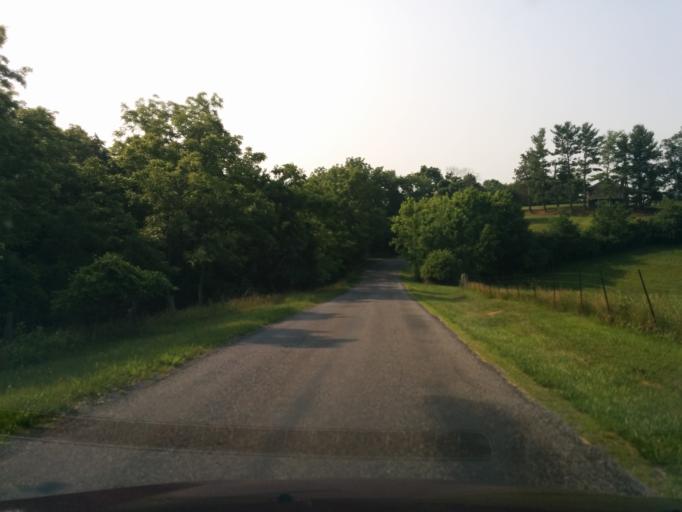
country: US
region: Virginia
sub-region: City of Lexington
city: Lexington
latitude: 37.7572
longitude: -79.4402
